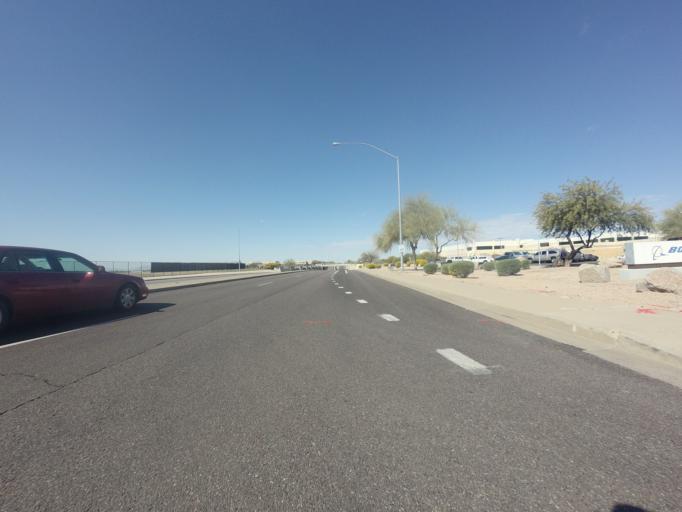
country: US
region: Arizona
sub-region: Maricopa County
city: Mesa
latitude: 33.4665
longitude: -111.7240
